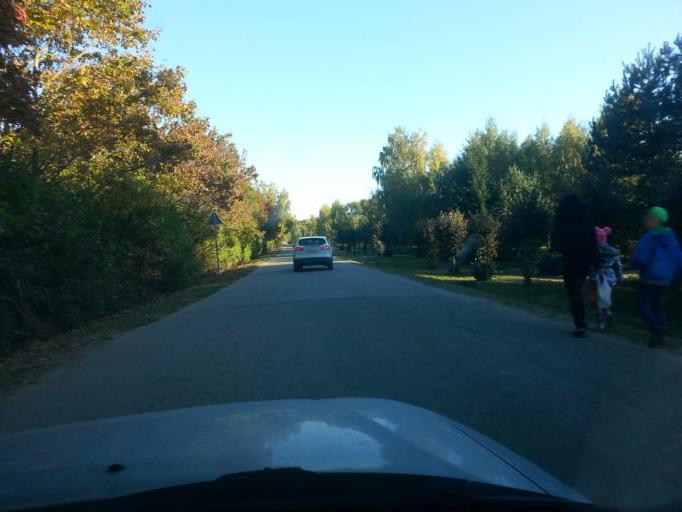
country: LV
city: Tervete
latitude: 56.6187
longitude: 23.4467
